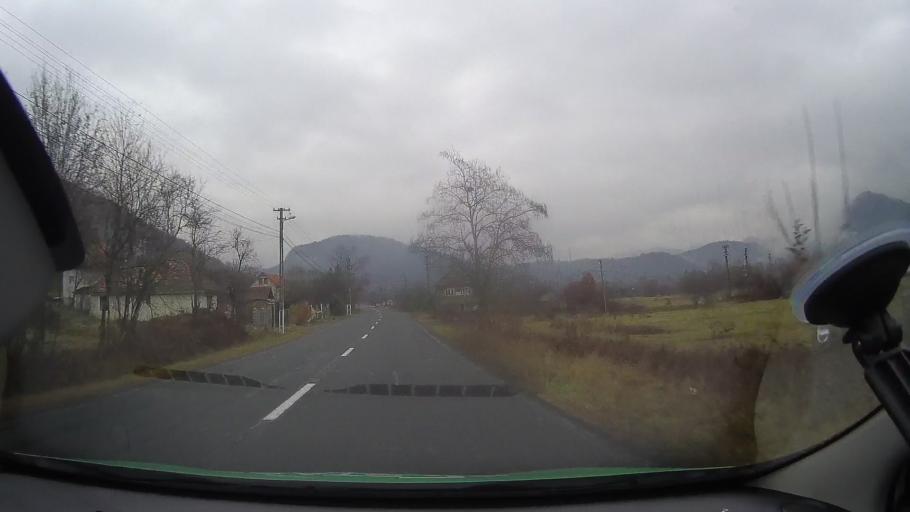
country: RO
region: Arad
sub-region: Comuna Plescuta
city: Plescuta
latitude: 46.2956
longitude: 22.4340
